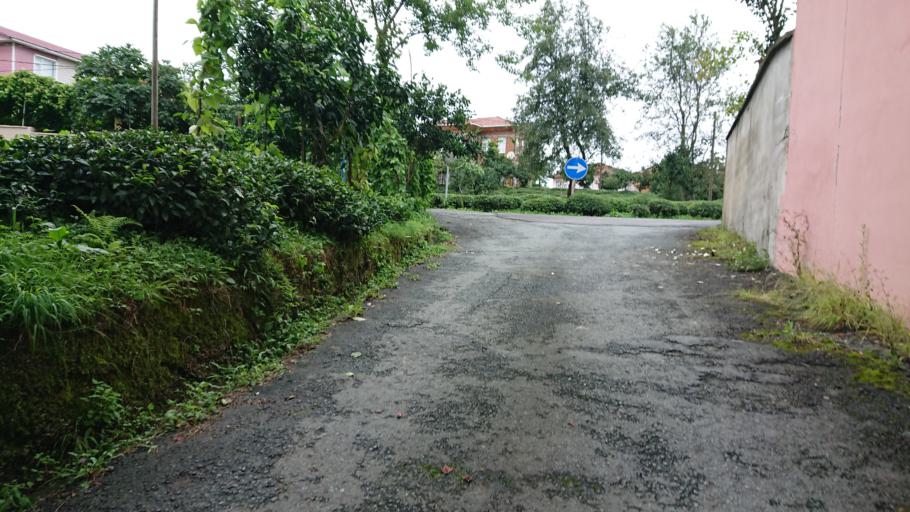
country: TR
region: Rize
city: Rize
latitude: 40.9836
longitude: 40.4849
